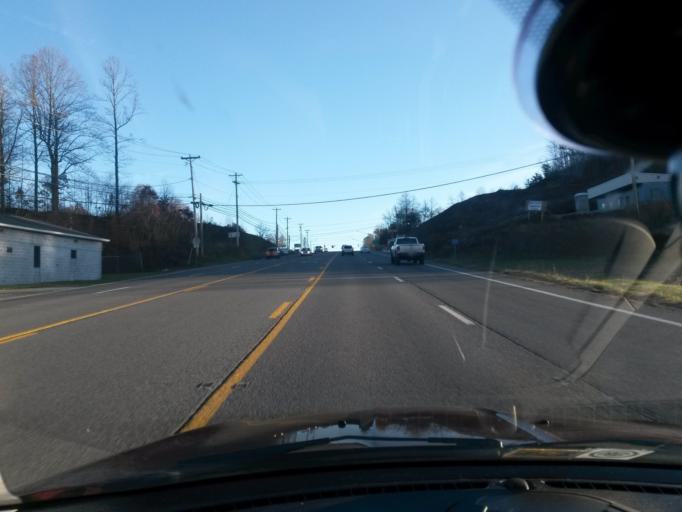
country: US
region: West Virginia
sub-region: Raleigh County
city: Prosperity
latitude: 37.8453
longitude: -81.1948
